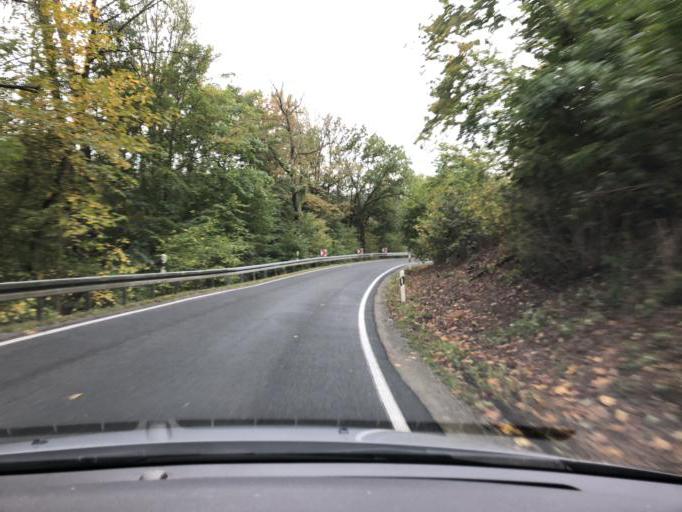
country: DE
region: Thuringia
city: Grossbartloff
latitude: 51.2542
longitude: 10.2348
